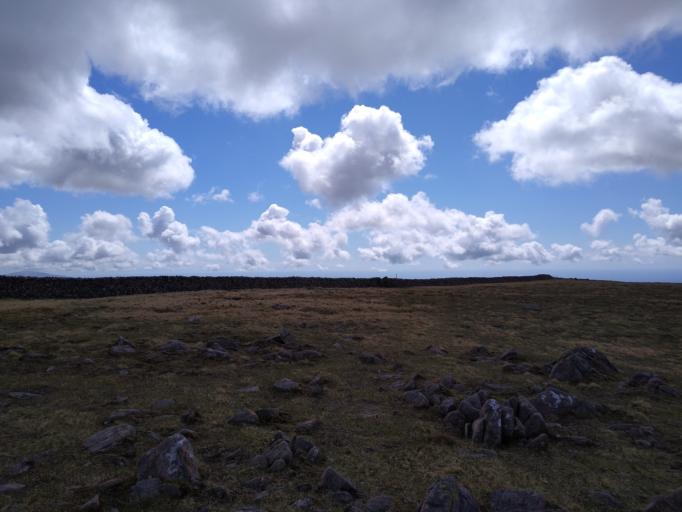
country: GB
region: England
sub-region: Cumbria
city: Frizington
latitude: 54.4869
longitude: -3.3415
